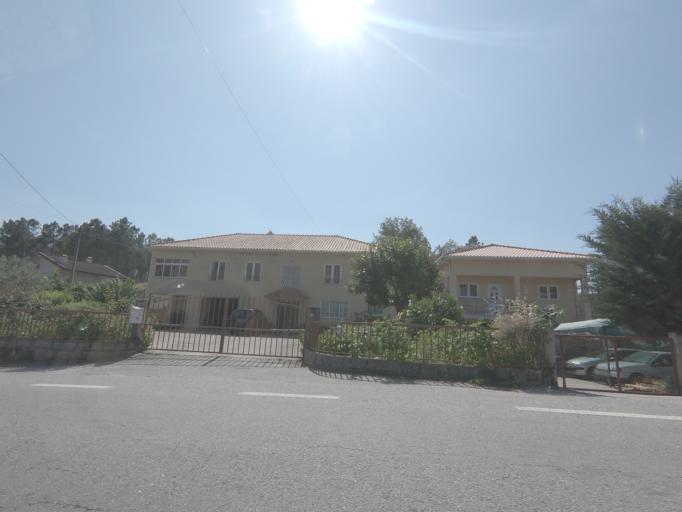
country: PT
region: Viseu
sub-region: Tarouca
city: Tarouca
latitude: 41.0275
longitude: -7.7458
